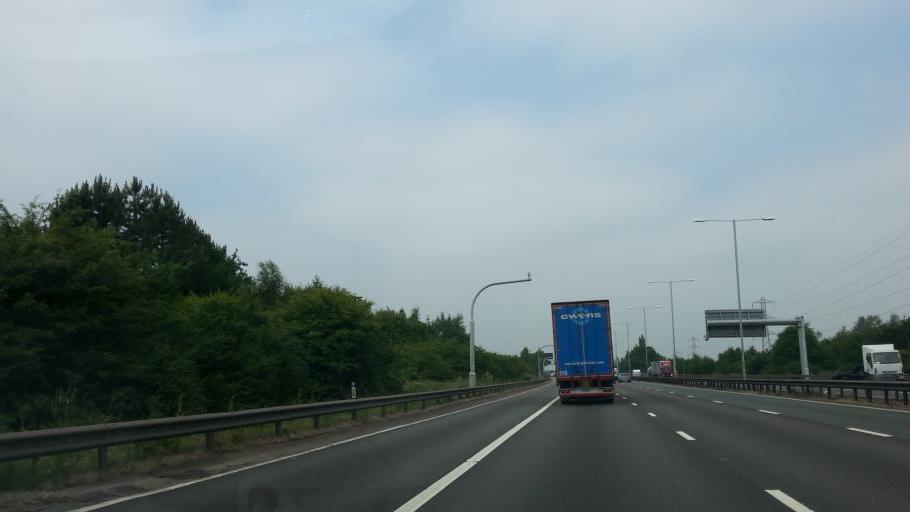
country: GB
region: England
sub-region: Walsall
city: Bloxwich
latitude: 52.6046
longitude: -2.0193
